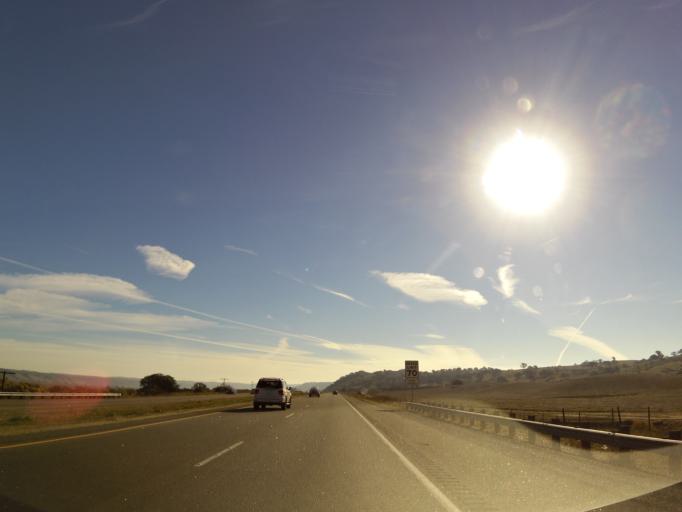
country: US
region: California
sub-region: San Luis Obispo County
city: Lake Nacimiento
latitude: 35.8688
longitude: -120.8264
